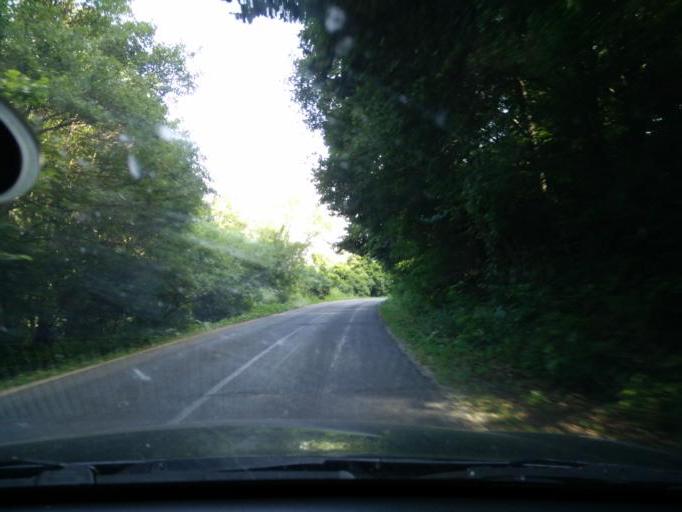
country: HU
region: Komarom-Esztergom
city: Tardos
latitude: 47.6692
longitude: 18.4438
